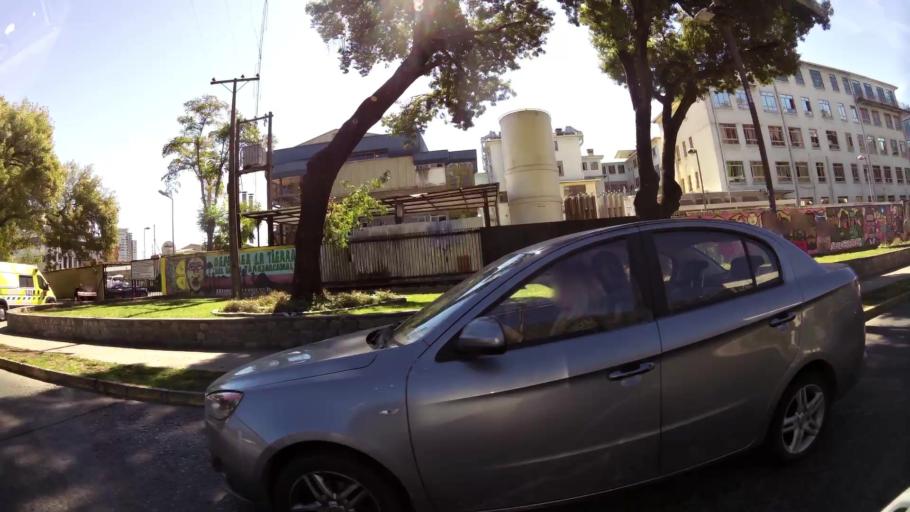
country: CL
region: Biobio
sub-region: Provincia de Concepcion
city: Concepcion
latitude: -36.8257
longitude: -73.0372
